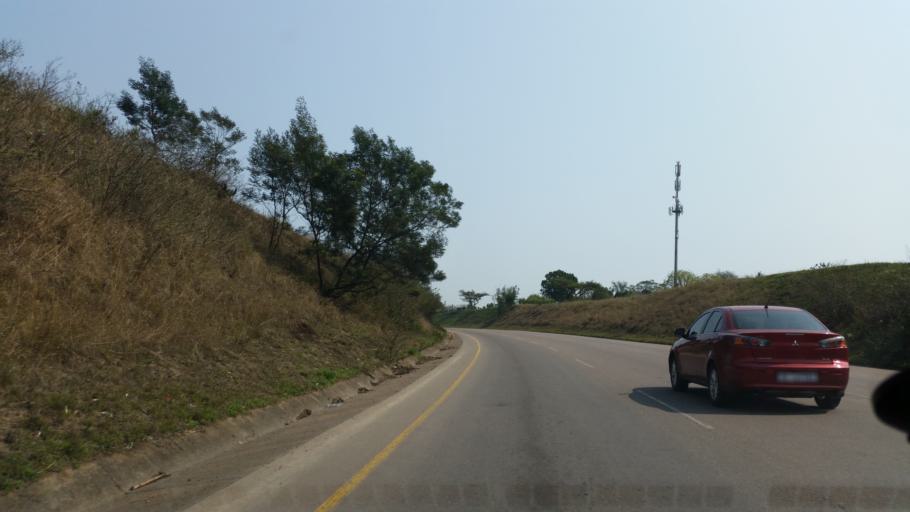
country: ZA
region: KwaZulu-Natal
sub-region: eThekwini Metropolitan Municipality
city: Mpumalanga
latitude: -29.7297
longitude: 30.6485
